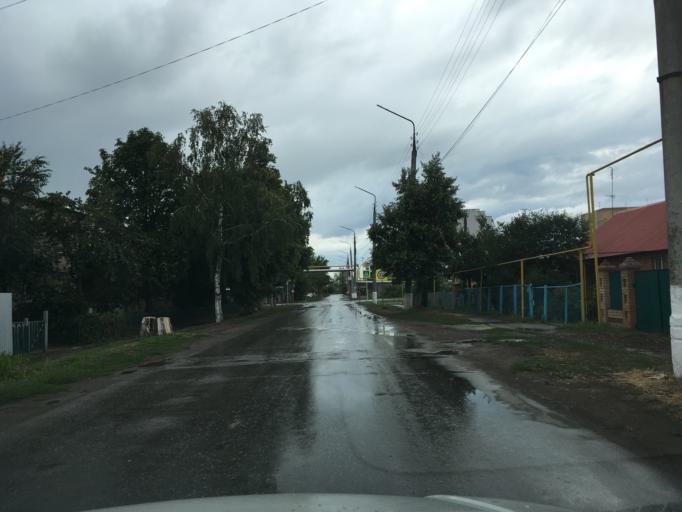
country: RU
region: Samara
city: Bezenchuk
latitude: 52.9820
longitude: 49.4392
